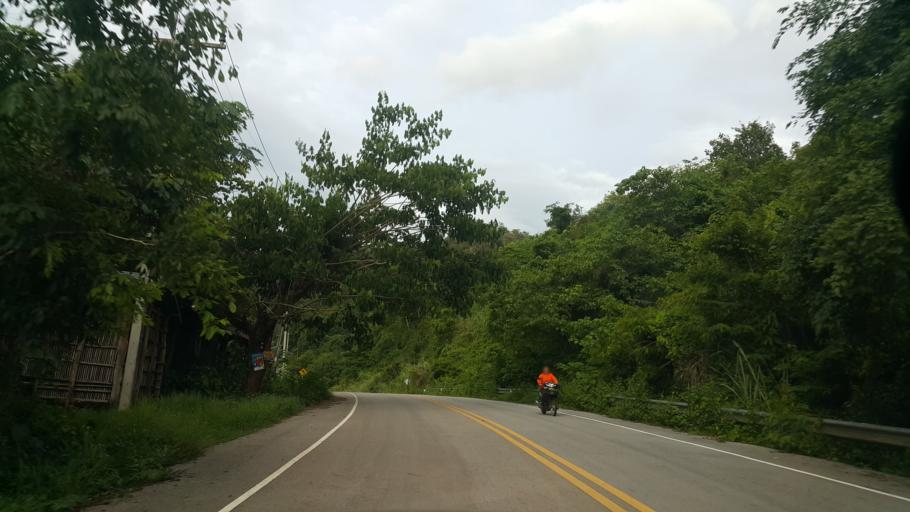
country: TH
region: Loei
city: Na Haeo
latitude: 17.4981
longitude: 101.0804
